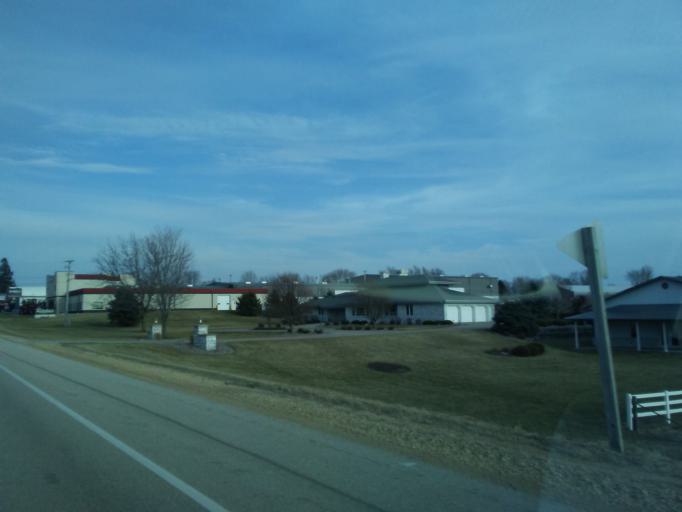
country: US
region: Wisconsin
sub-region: Iowa County
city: Mineral Point
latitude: 42.9672
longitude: -90.3391
